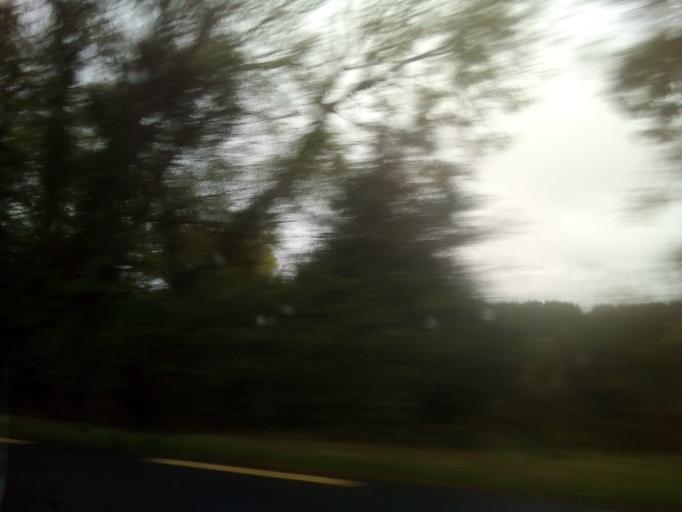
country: IE
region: Connaught
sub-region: Roscommon
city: Castlerea
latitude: 53.8529
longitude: -8.3911
